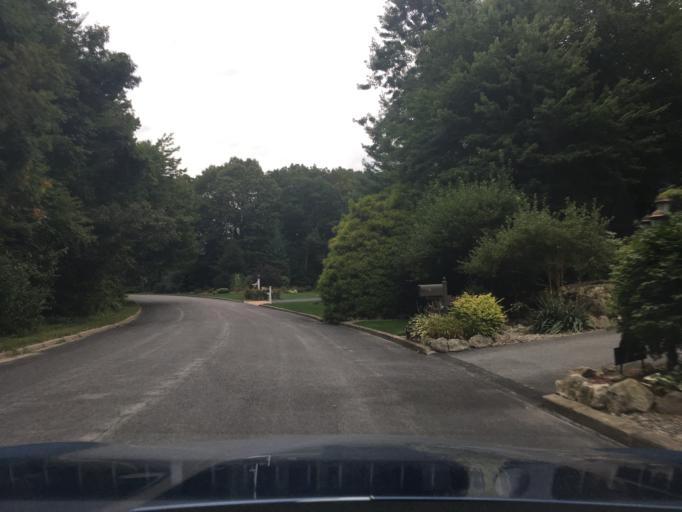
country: US
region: Rhode Island
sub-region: Kent County
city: East Greenwich
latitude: 41.6329
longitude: -71.5061
